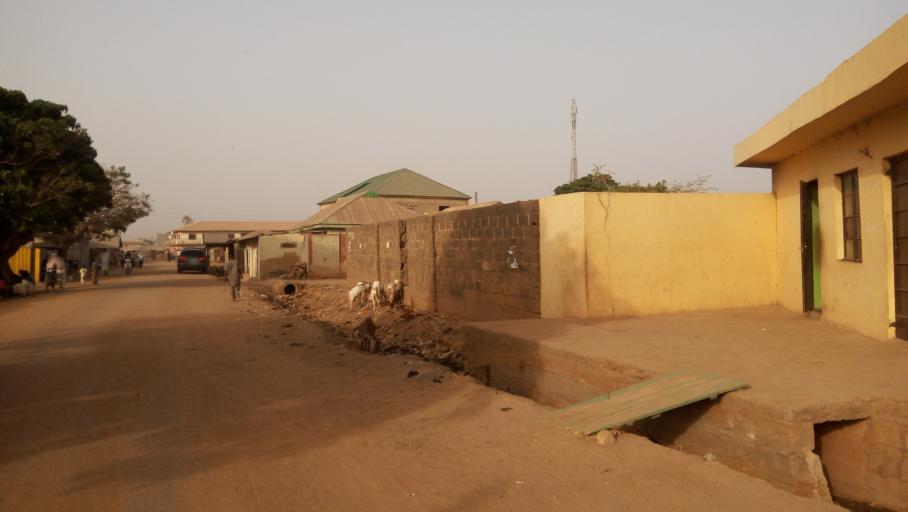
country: NG
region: Kaduna
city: Zaria
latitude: 11.1645
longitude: 7.6510
